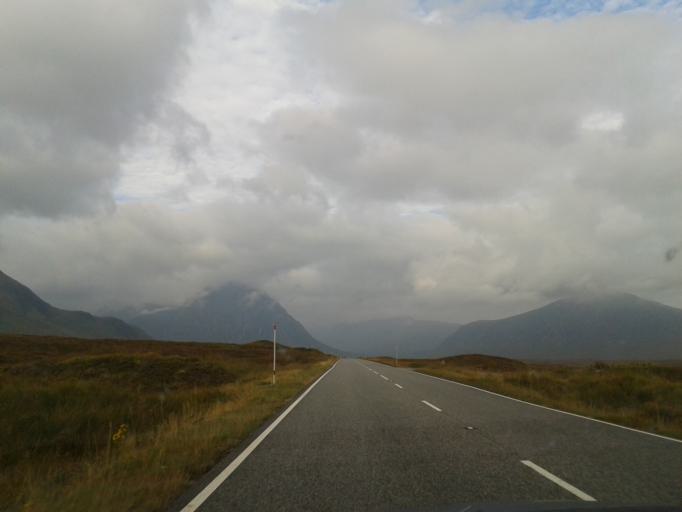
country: GB
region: Scotland
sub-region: Highland
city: Spean Bridge
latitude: 56.6330
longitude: -4.7936
